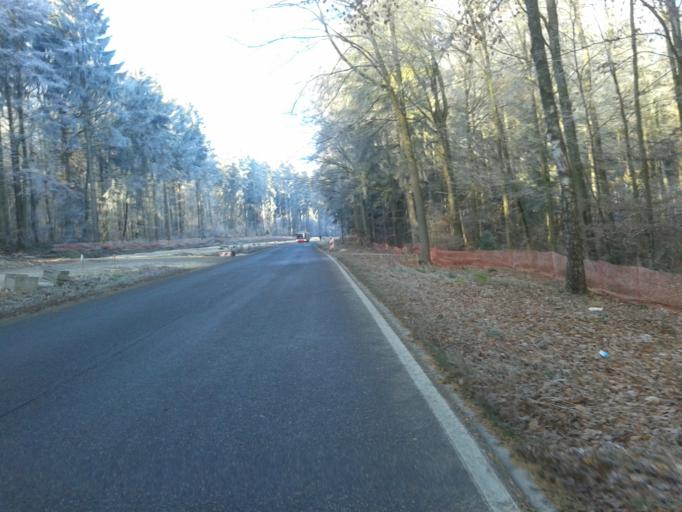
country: DE
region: Baden-Wuerttemberg
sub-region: Tuebingen Region
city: Ulm
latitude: 48.4194
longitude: 9.9608
